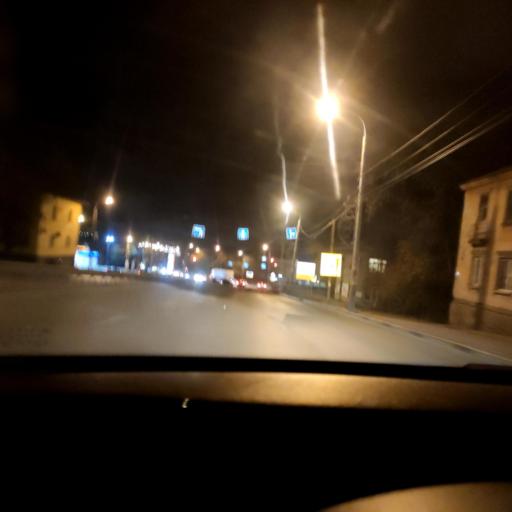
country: RU
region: Samara
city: Samara
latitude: 53.1806
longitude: 50.1918
